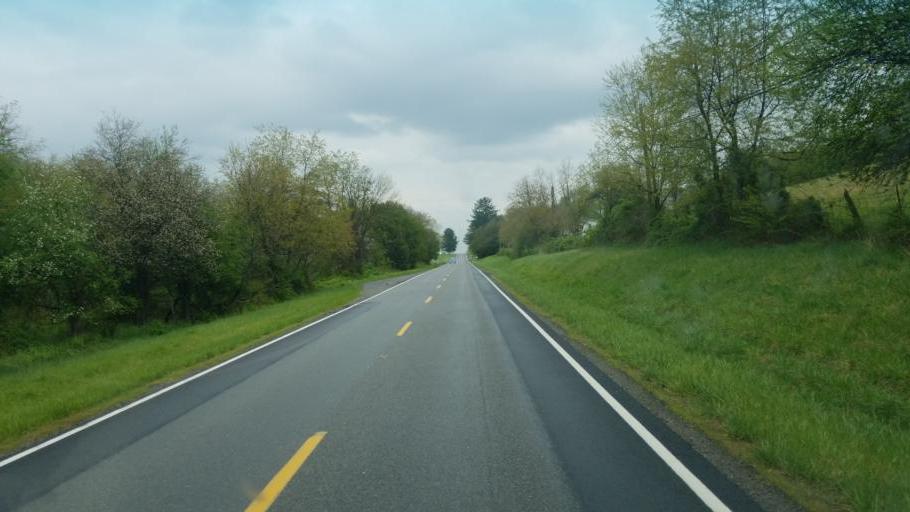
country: US
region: Virginia
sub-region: Wythe County
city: Rural Retreat
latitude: 36.9004
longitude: -81.3215
